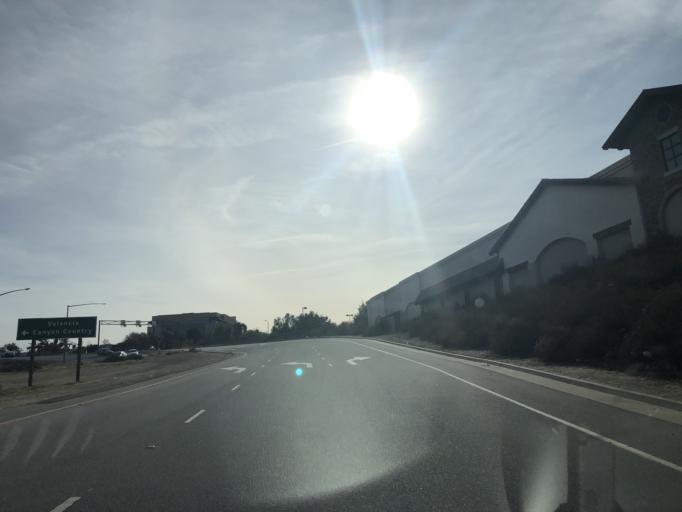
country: US
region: California
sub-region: Los Angeles County
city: Santa Clarita
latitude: 34.4096
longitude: -118.5778
